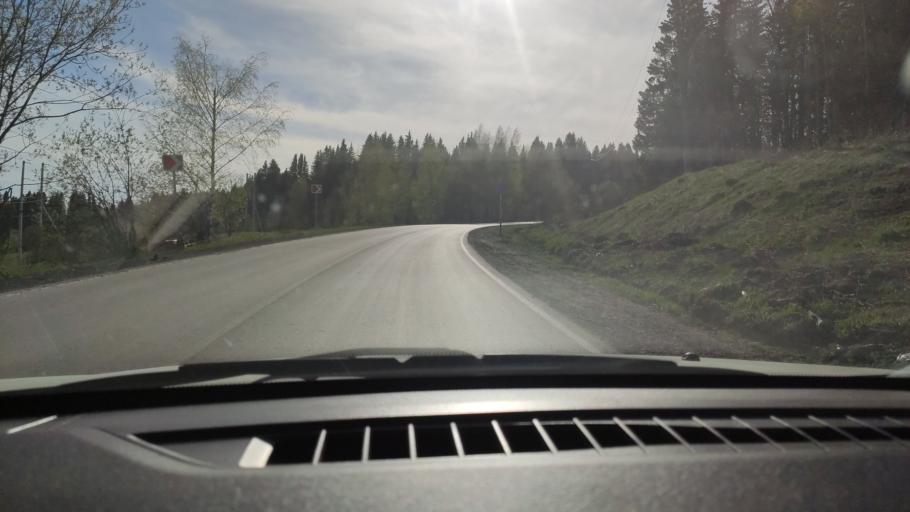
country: RU
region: Perm
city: Novyye Lyady
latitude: 57.9209
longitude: 56.6612
